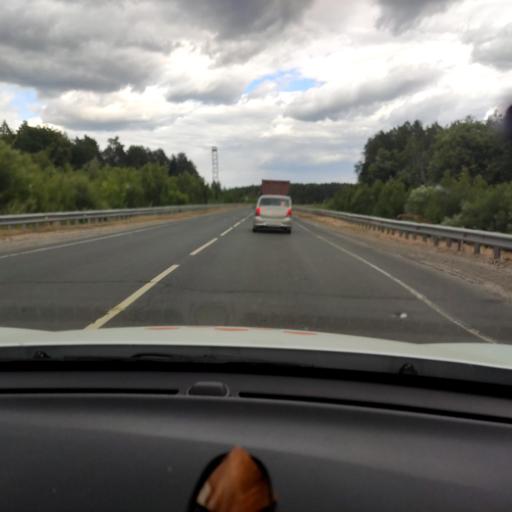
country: RU
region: Mariy-El
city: Yoshkar-Ola
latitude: 56.5422
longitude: 47.9711
